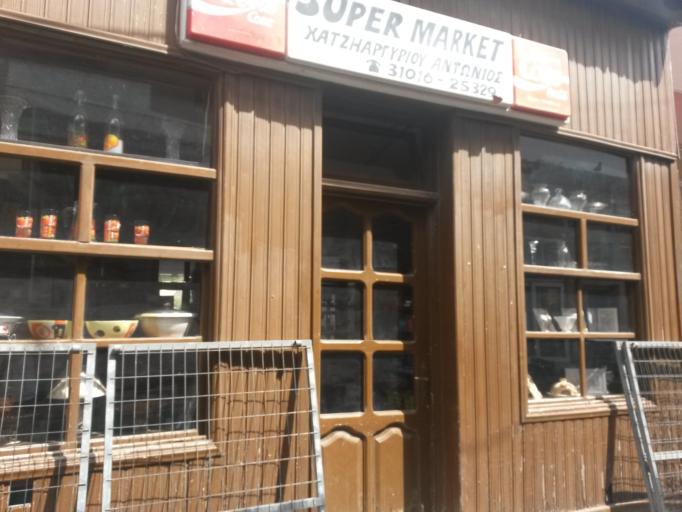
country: GR
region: North Aegean
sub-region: Nomos Lesvou
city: Moria
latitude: 39.1323
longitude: 26.5174
